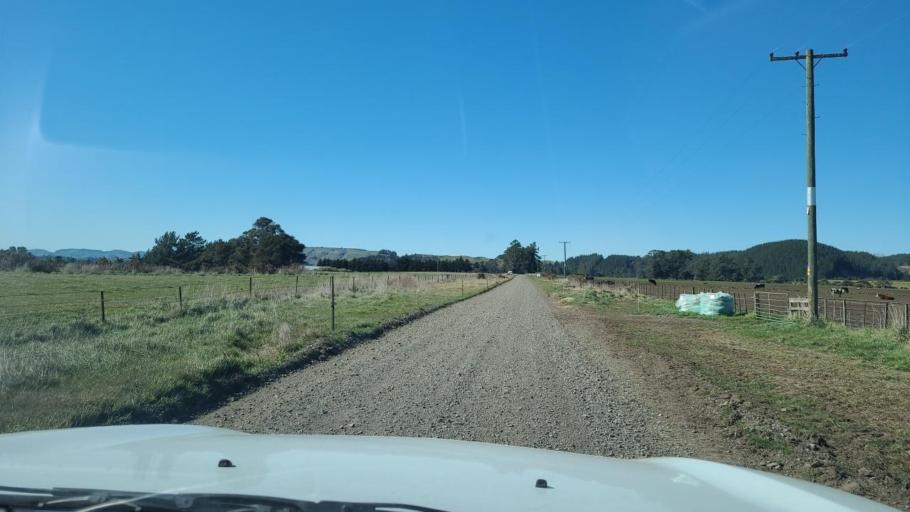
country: NZ
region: Hawke's Bay
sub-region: Napier City
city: Taradale
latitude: -39.4620
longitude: 176.5831
